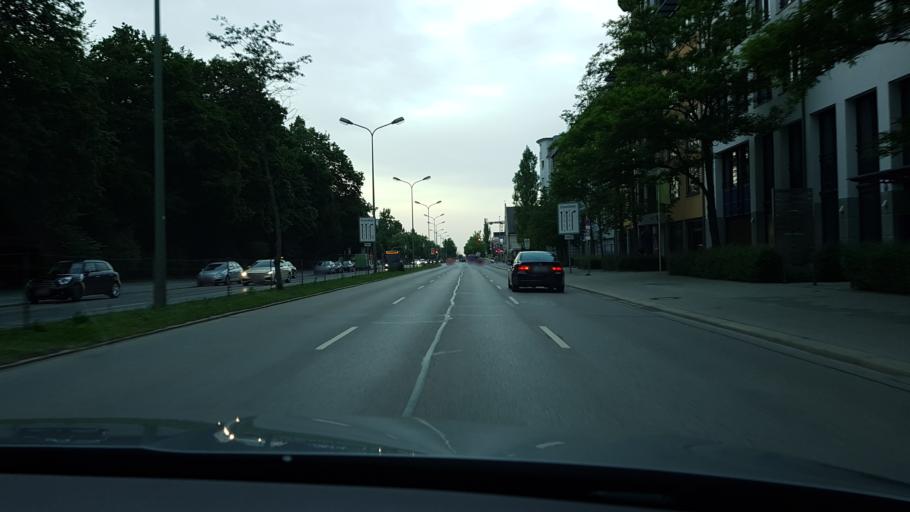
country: DE
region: Bavaria
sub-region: Upper Bavaria
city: Neuried
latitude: 48.1102
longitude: 11.5023
